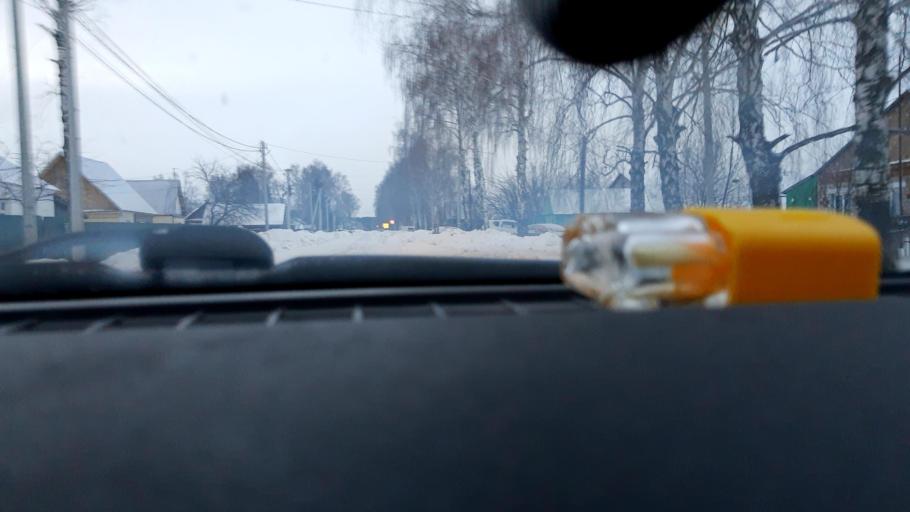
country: RU
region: Bashkortostan
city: Iglino
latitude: 54.8050
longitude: 56.4261
